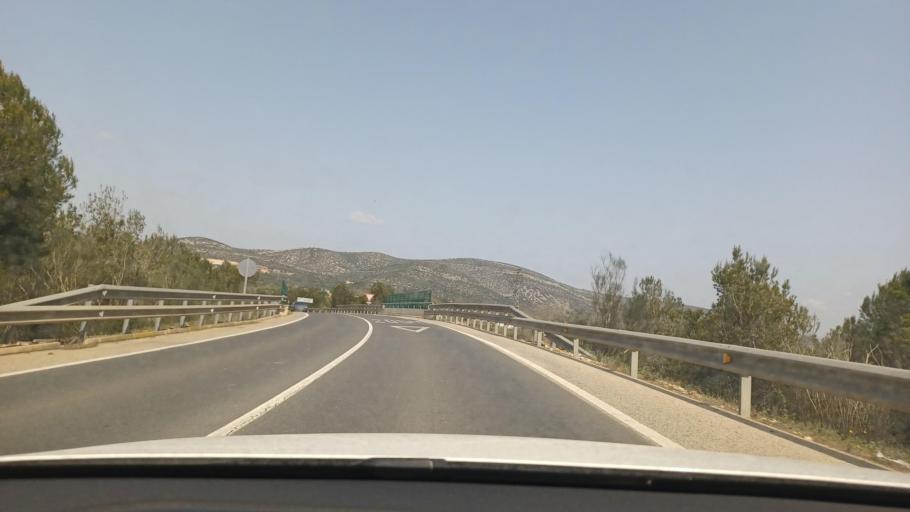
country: ES
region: Catalonia
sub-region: Provincia de Tarragona
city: Ulldecona
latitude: 40.6006
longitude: 0.4555
